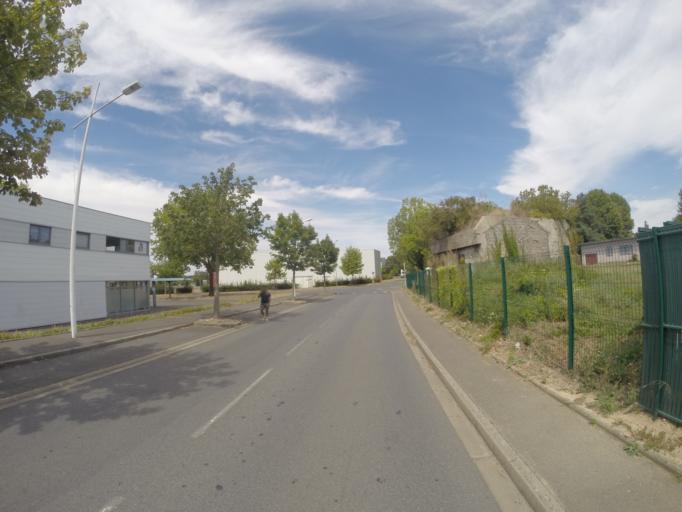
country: FR
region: Centre
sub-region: Departement d'Indre-et-Loire
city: Chanceaux-sur-Choisille
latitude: 47.4309
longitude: 0.7074
